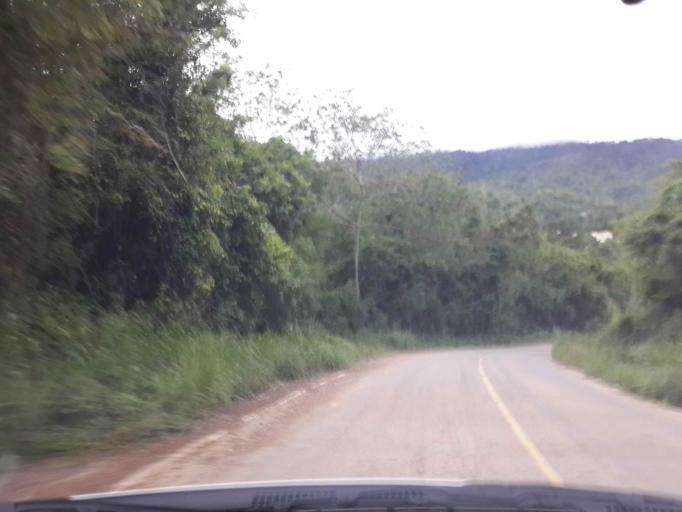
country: TH
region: Ratchaburi
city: Suan Phueng
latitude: 13.5858
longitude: 99.2162
